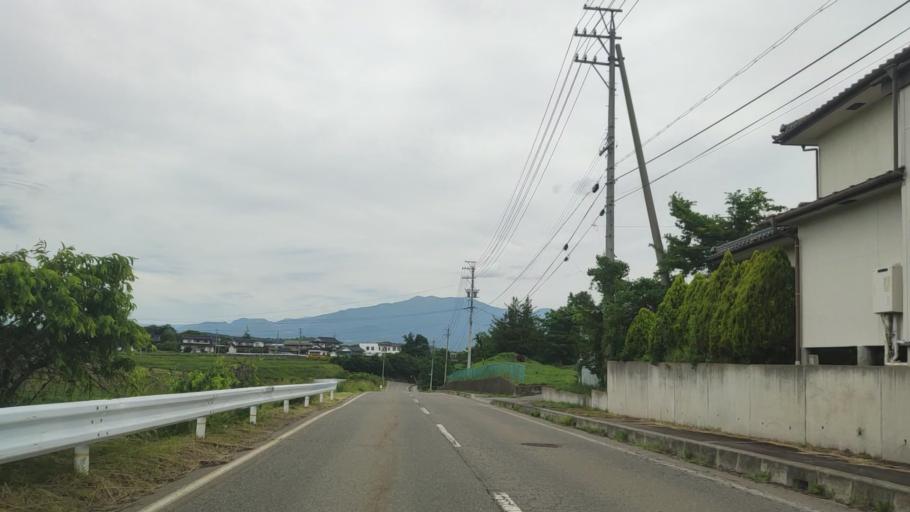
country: JP
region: Nagano
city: Kamimaruko
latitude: 36.2959
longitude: 138.3182
